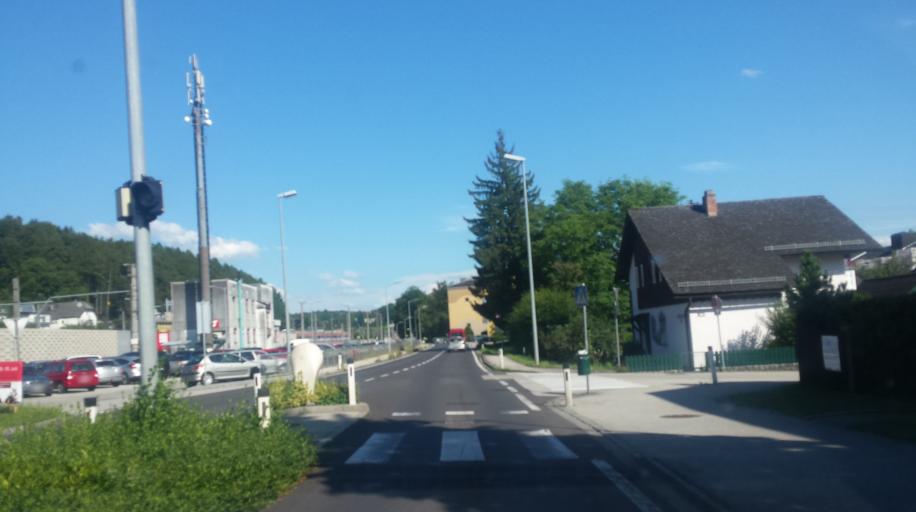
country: AT
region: Upper Austria
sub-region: Politischer Bezirk Vocklabruck
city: Vocklabruck
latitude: 48.0095
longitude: 13.6643
